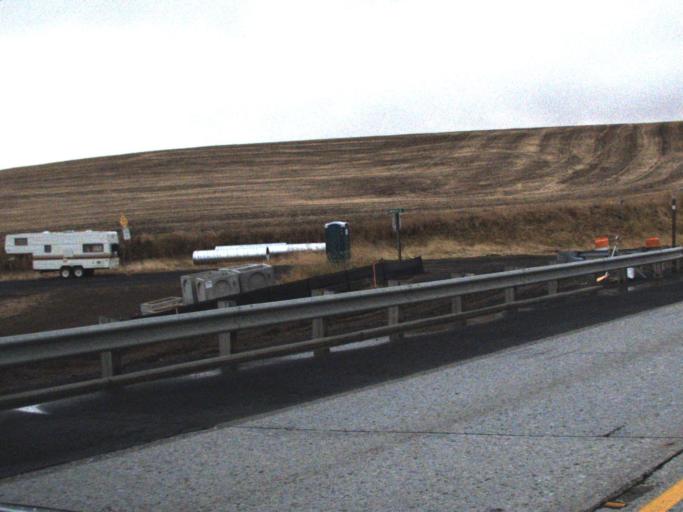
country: US
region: Washington
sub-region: Whitman County
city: Colfax
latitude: 47.0200
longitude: -117.3576
